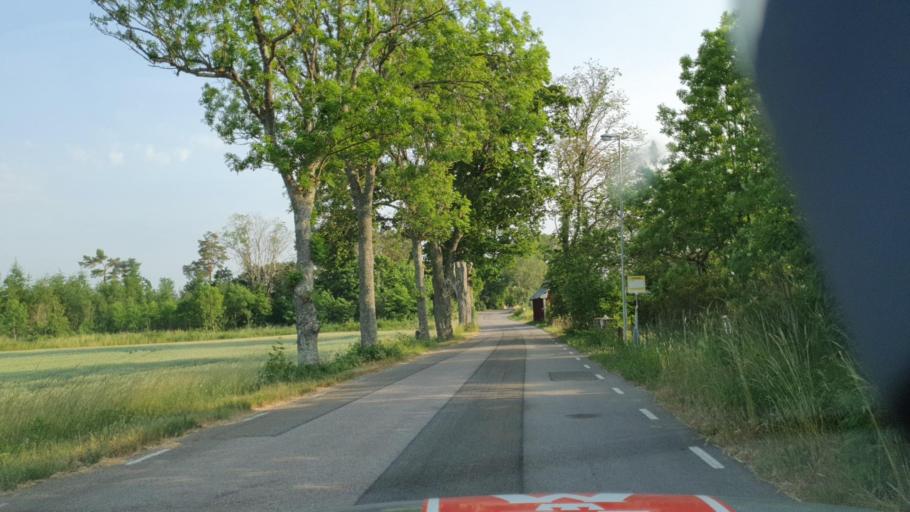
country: SE
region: Kalmar
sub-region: Kalmar Kommun
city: Ljungbyholm
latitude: 56.5106
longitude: 16.1259
